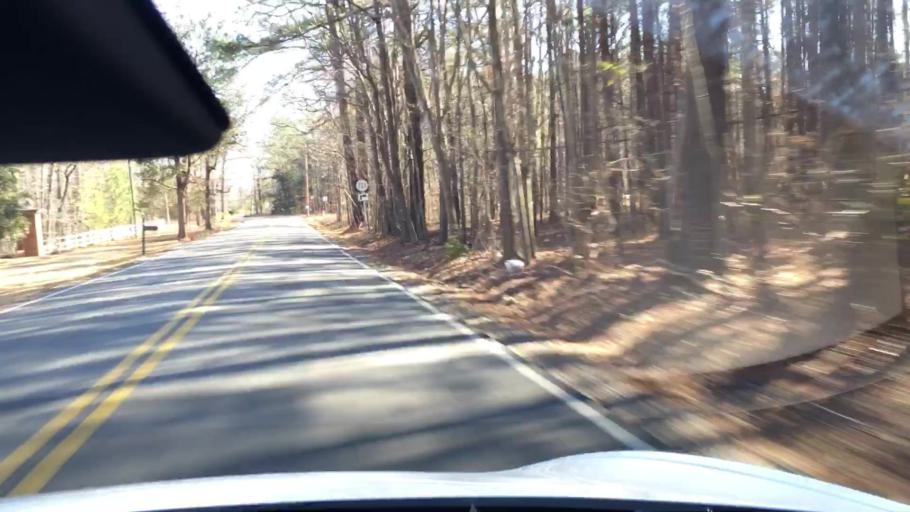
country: US
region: Virginia
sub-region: Henrico County
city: Short Pump
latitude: 37.5624
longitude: -77.6996
